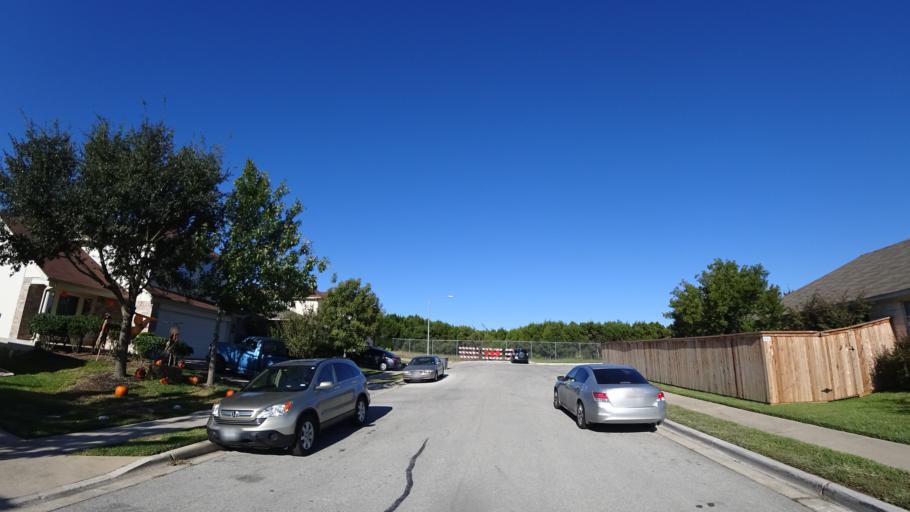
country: US
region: Texas
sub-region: Travis County
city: Austin
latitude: 30.2903
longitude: -97.6702
